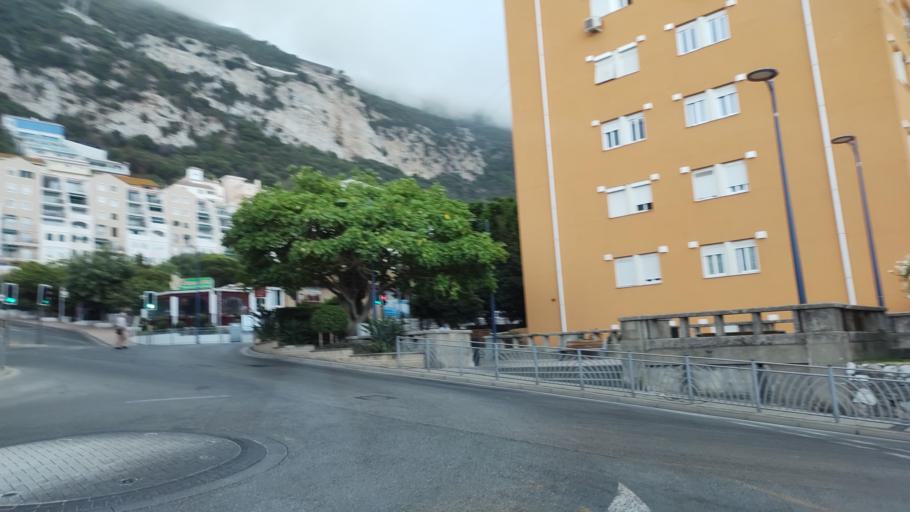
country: GI
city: Gibraltar
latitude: 36.1338
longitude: -5.3526
